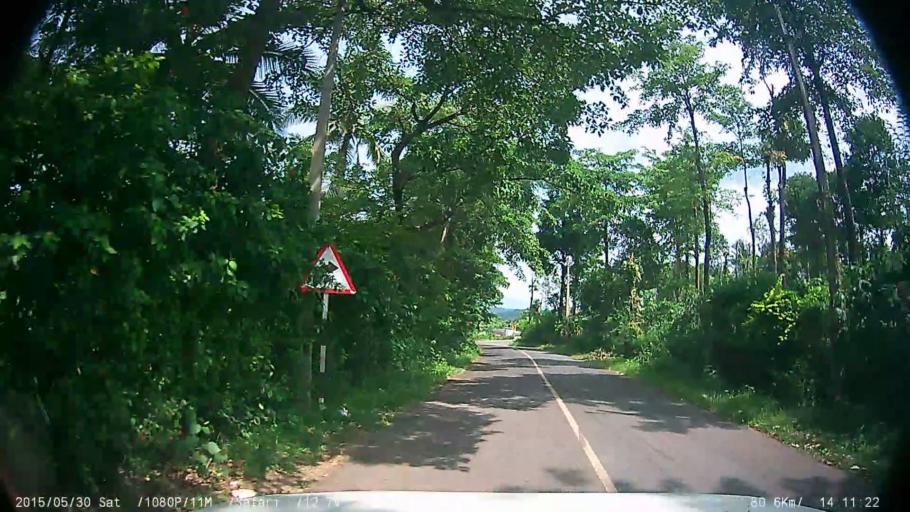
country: IN
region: Kerala
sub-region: Wayanad
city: Panamaram
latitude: 11.7925
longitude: 76.0536
